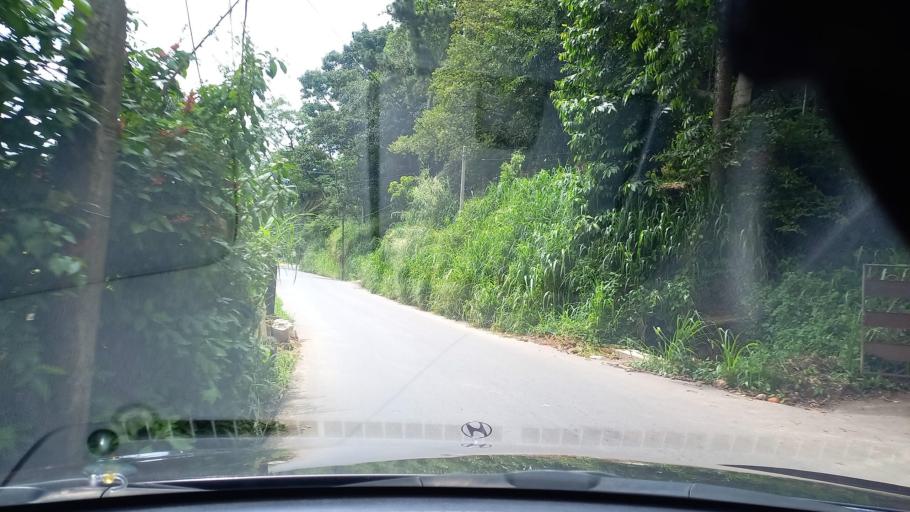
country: LK
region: Central
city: Kandy
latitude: 7.2331
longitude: 80.6039
